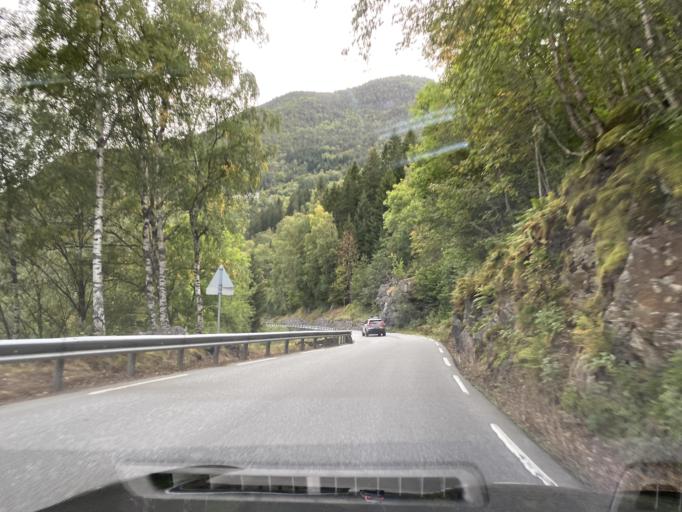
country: NO
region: Hordaland
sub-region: Odda
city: Odda
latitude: 60.1588
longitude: 6.5754
